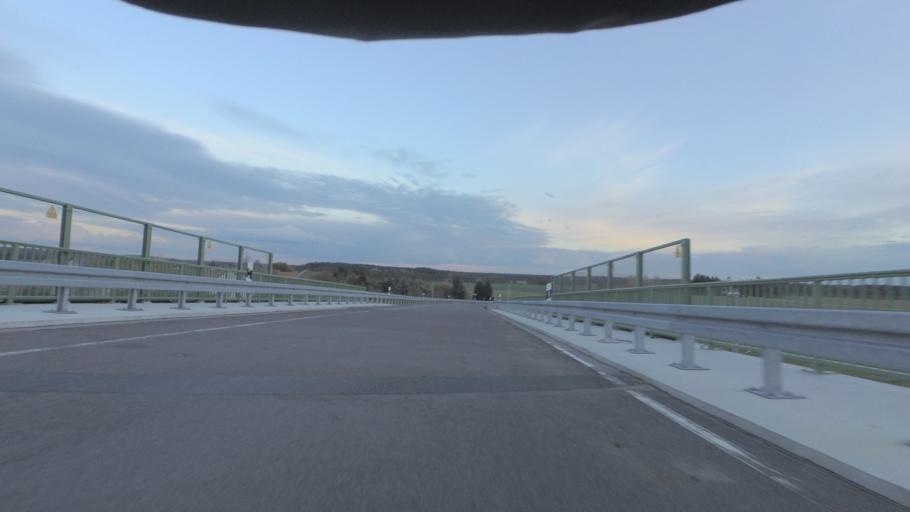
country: DE
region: Brandenburg
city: Sonnewalde
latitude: 51.7551
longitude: 13.6111
